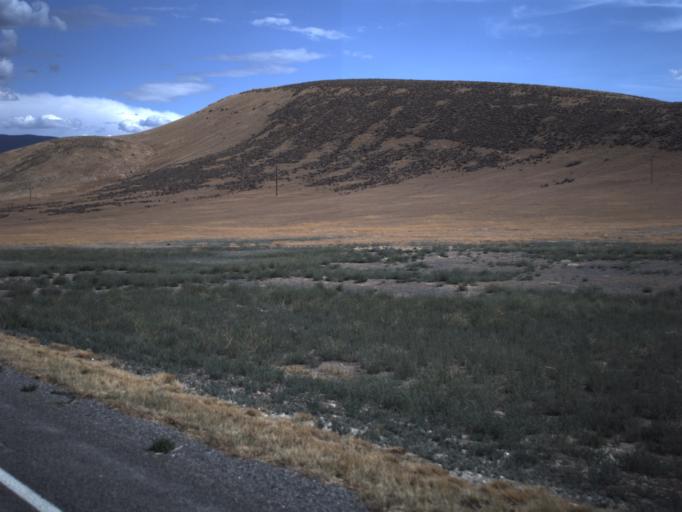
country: US
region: Utah
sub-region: Sanpete County
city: Gunnison
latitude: 39.1575
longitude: -111.7780
